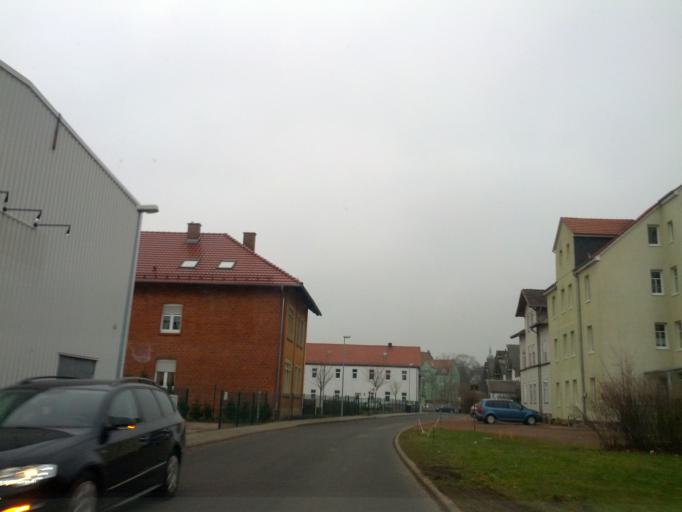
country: DE
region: Thuringia
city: Eisenach
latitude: 50.9782
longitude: 10.3111
